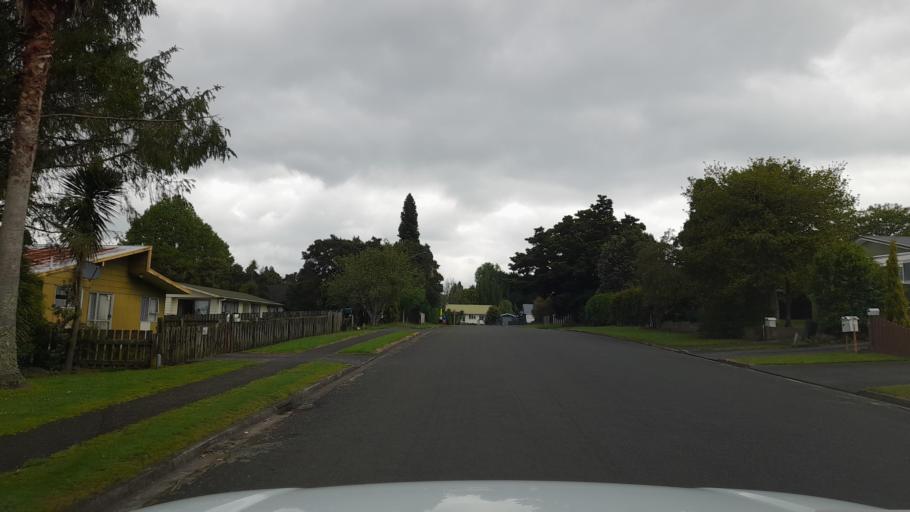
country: NZ
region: Northland
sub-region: Far North District
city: Waimate North
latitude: -35.4030
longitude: 173.7966
